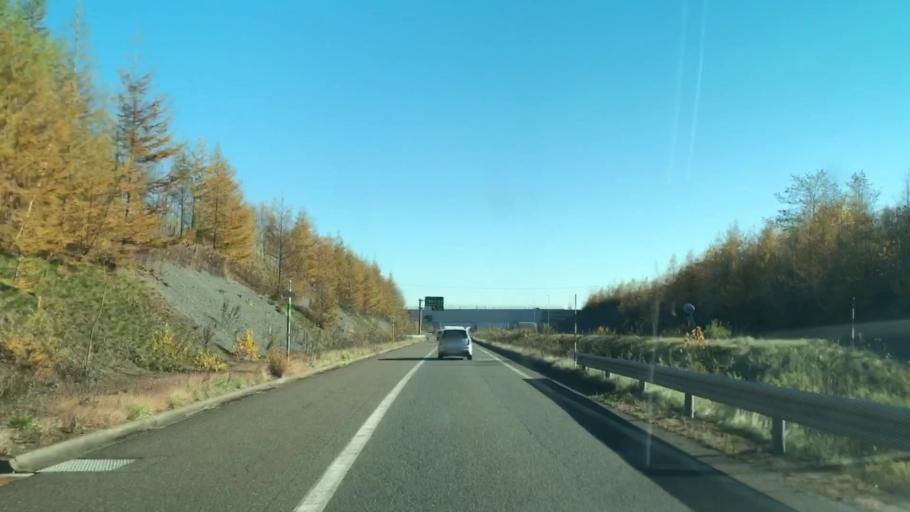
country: JP
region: Hokkaido
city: Otofuke
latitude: 42.9983
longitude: 142.8524
